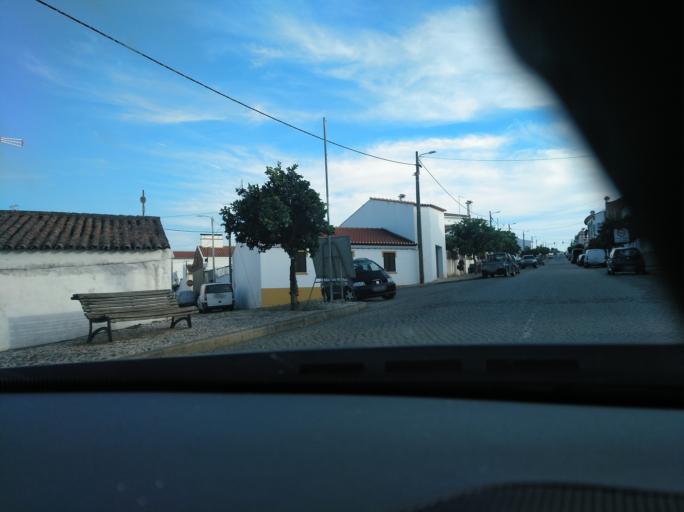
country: PT
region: Portalegre
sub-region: Fronteira
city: Fronteira
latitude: 38.9566
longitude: -7.6748
